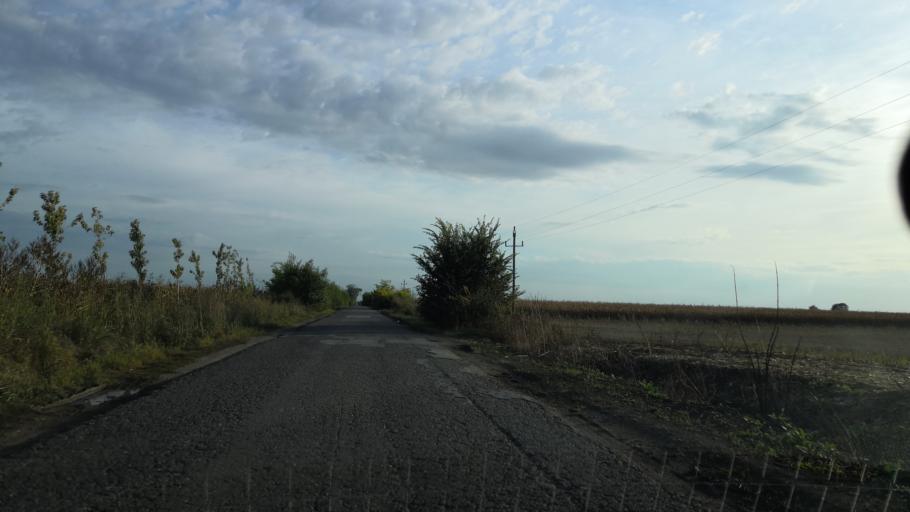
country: RS
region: Autonomna Pokrajina Vojvodina
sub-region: Sremski Okrug
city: Stara Pazova
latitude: 45.0222
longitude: 20.1702
